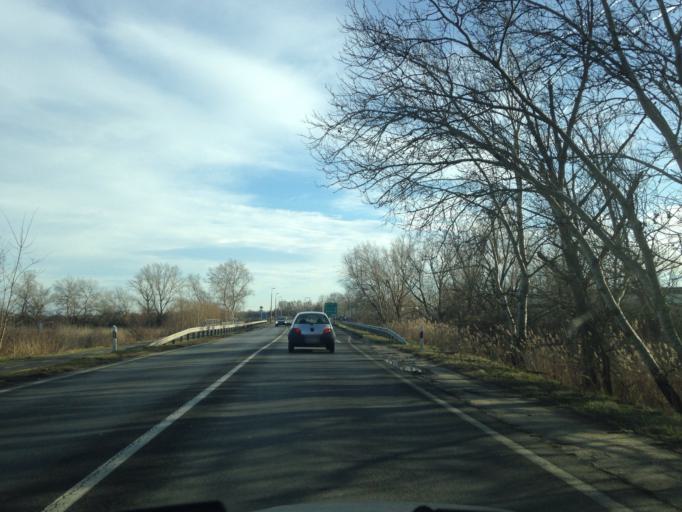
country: HU
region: Gyor-Moson-Sopron
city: Abda
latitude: 47.6852
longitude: 17.5671
